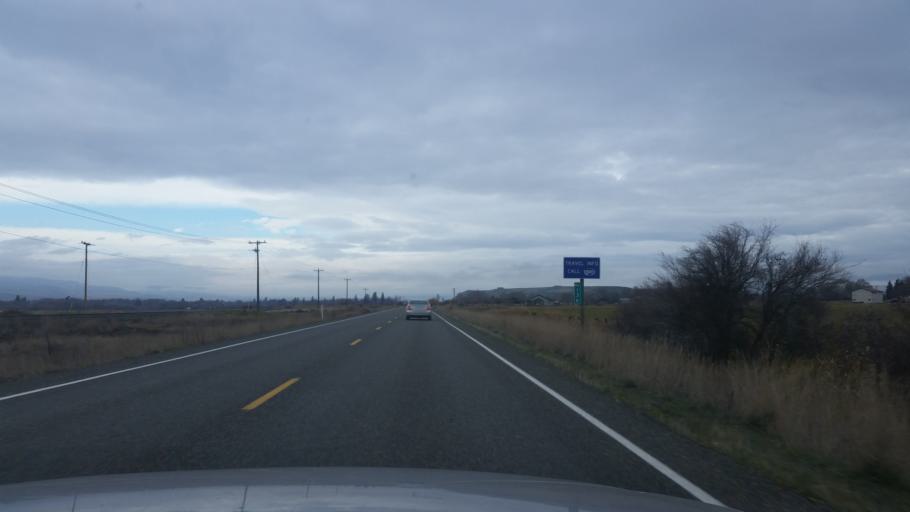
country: US
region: Washington
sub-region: Kittitas County
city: Ellensburg
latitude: 47.0283
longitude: -120.6017
